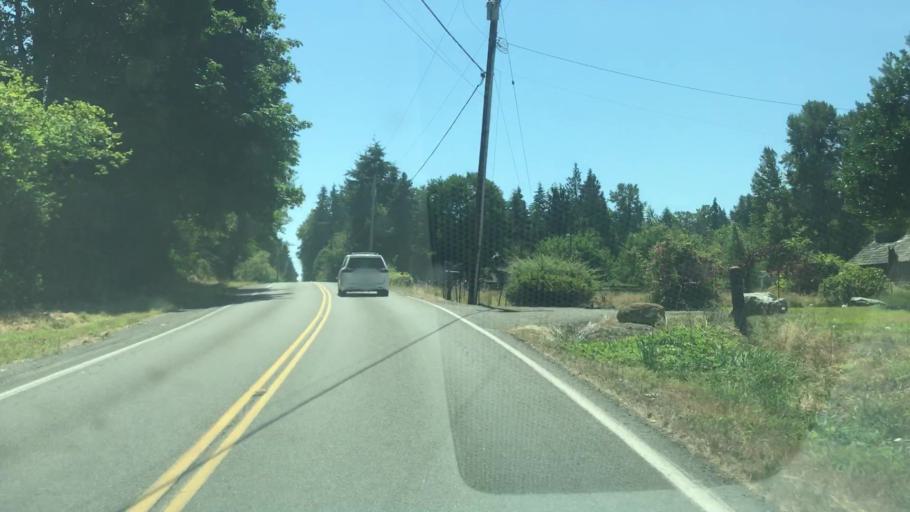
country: US
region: Washington
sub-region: Snohomish County
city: Cathcart
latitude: 47.8278
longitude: -122.0773
